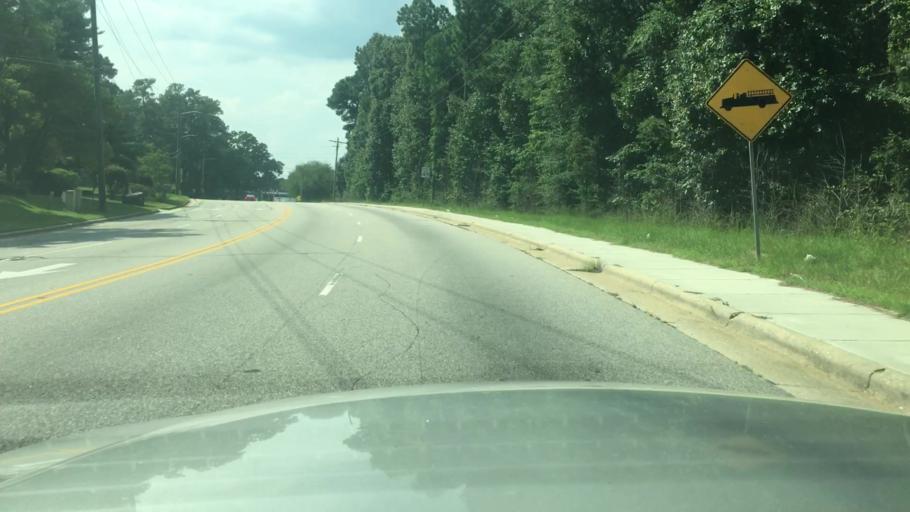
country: US
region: North Carolina
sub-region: Cumberland County
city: Fayetteville
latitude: 35.1014
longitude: -78.8960
